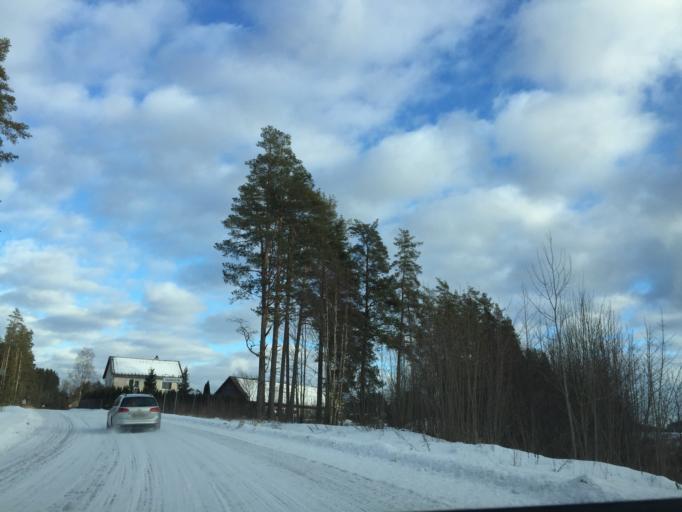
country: LV
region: Ogre
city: Jumprava
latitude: 56.5634
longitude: 24.9190
